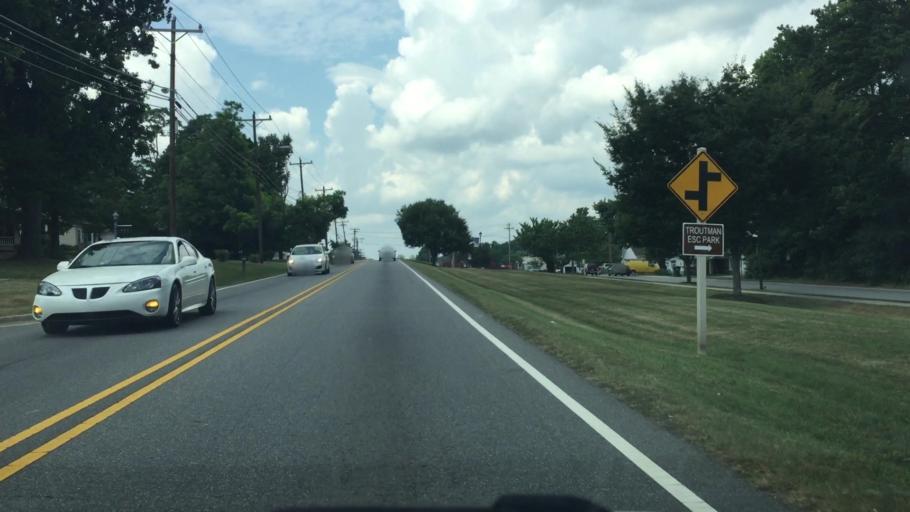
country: US
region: North Carolina
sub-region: Iredell County
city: Troutman
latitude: 35.7084
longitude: -80.8939
